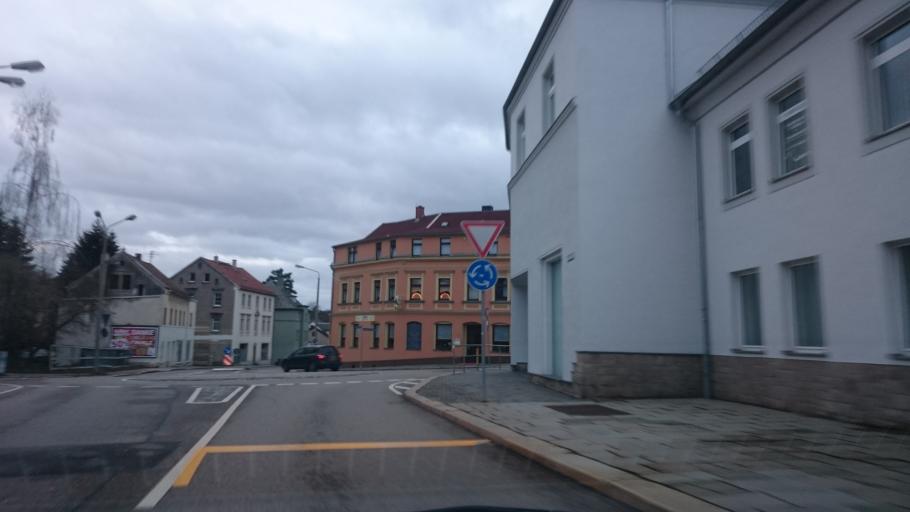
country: DE
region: Saxony
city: Wilkau-Hasslau
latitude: 50.6836
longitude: 12.4738
